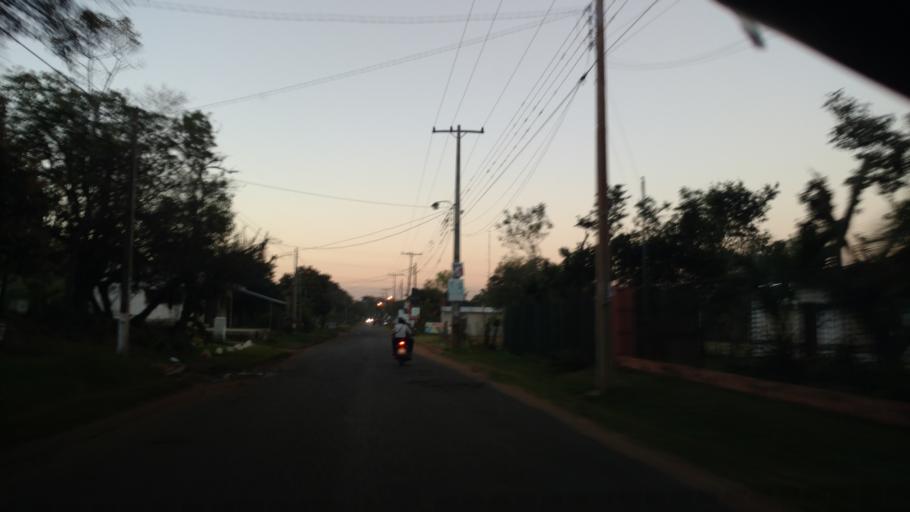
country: PY
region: Central
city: Guarambare
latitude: -25.4717
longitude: -57.4108
